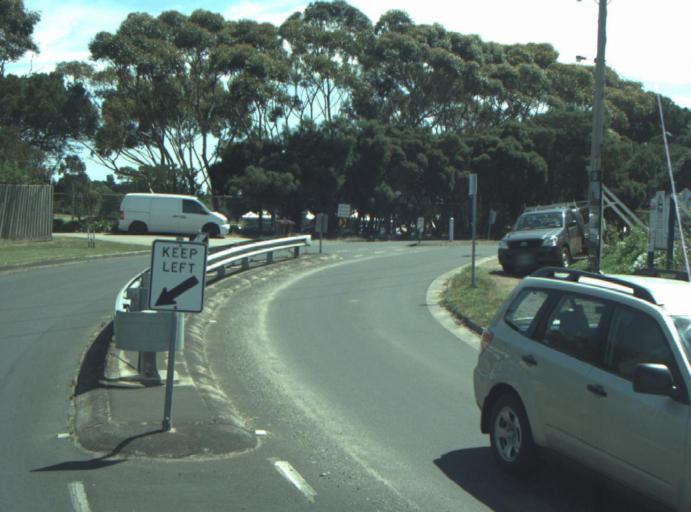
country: AU
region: Victoria
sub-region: Greater Geelong
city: Geelong West
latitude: -38.1481
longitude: 144.3271
